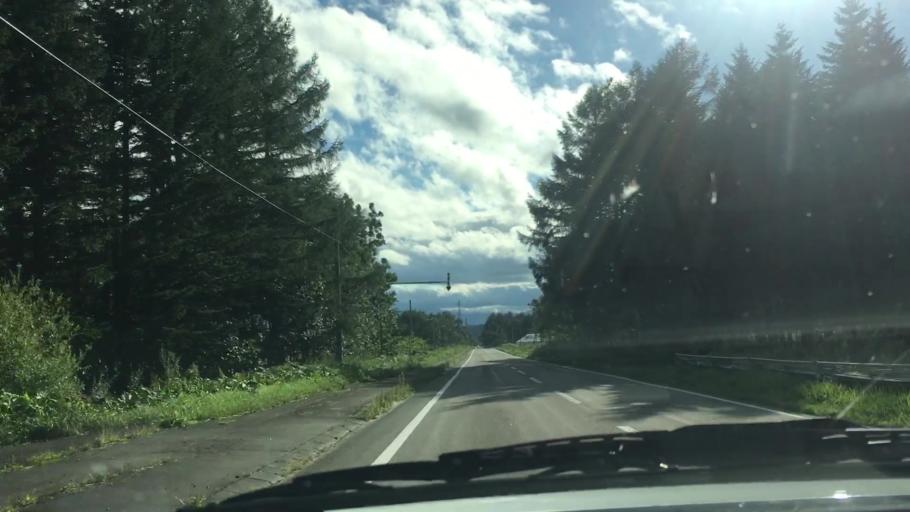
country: JP
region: Hokkaido
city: Otofuke
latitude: 43.1844
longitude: 143.0201
